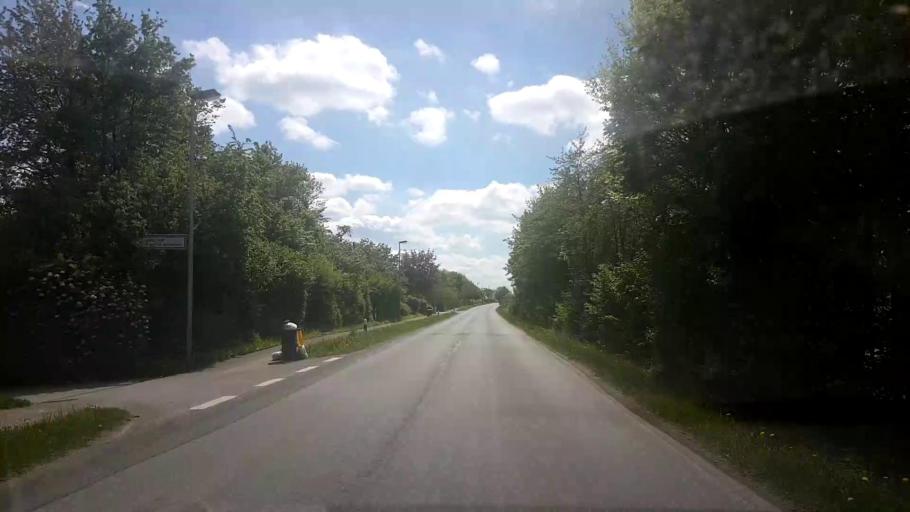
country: DE
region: Bavaria
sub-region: Upper Franconia
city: Untersiemau
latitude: 50.1939
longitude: 10.9624
